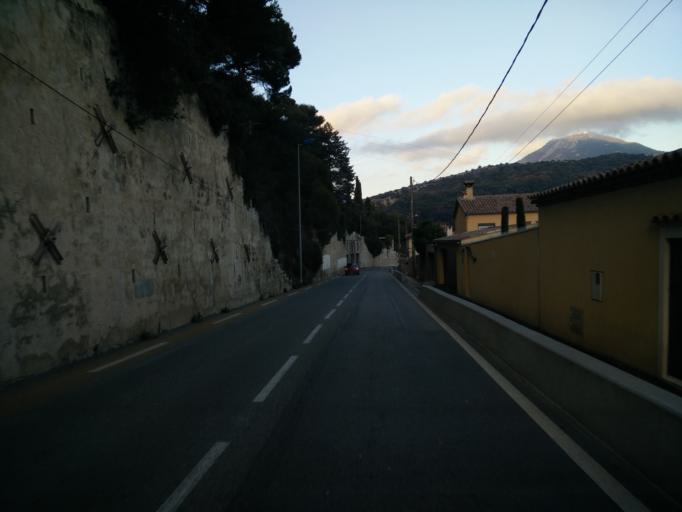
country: FR
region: Provence-Alpes-Cote d'Azur
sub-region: Departement des Alpes-Maritimes
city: La Turbie
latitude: 43.7415
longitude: 7.3909
